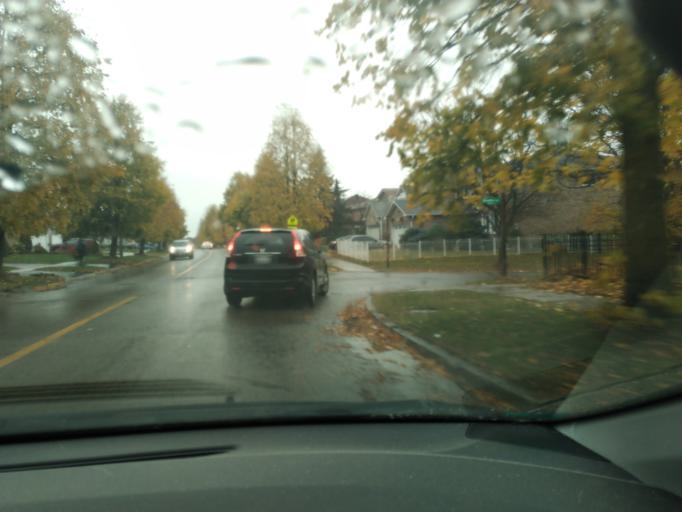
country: CA
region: Ontario
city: Markham
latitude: 43.8313
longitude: -79.2807
